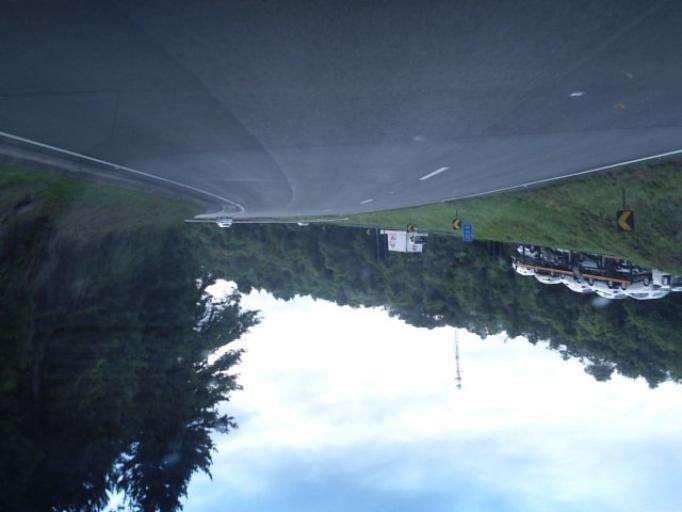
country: BR
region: Parana
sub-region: Campina Grande Do Sul
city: Campina Grande do Sul
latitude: -25.1912
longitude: -48.8851
